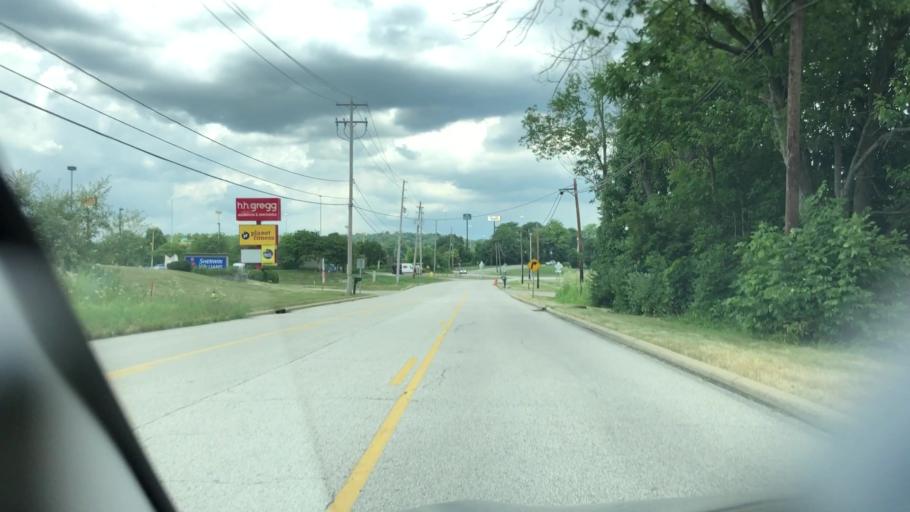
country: US
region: Ohio
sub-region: Summit County
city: Montrose-Ghent
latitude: 41.1309
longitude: -81.6484
